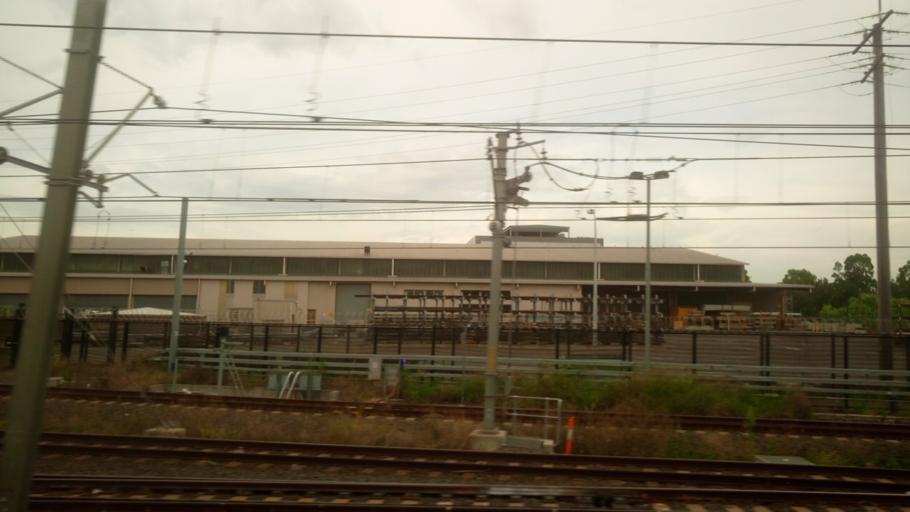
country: AU
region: New South Wales
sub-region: Parramatta
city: Granville
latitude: -33.8379
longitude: 151.0198
